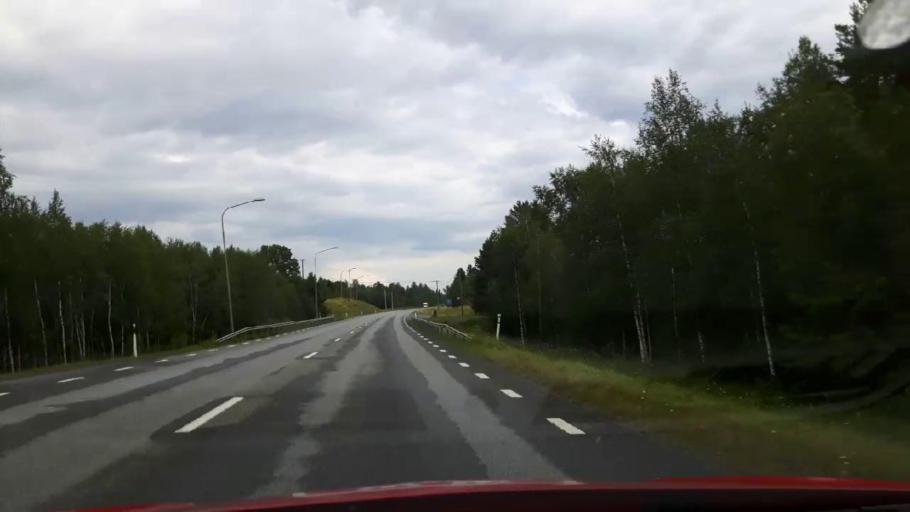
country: SE
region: Jaemtland
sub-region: Stroemsunds Kommun
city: Stroemsund
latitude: 63.6791
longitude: 15.3994
